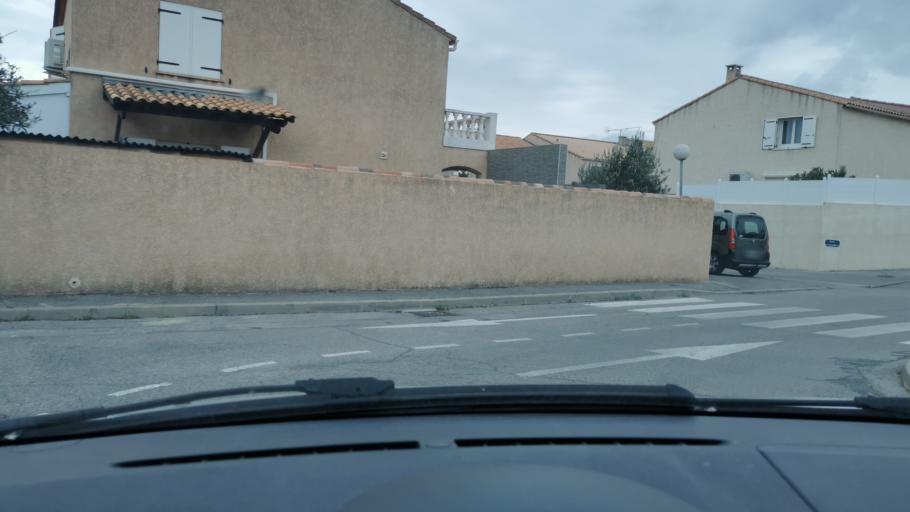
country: FR
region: Languedoc-Roussillon
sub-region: Departement de l'Herault
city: Frontignan
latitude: 43.4546
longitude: 3.7524
